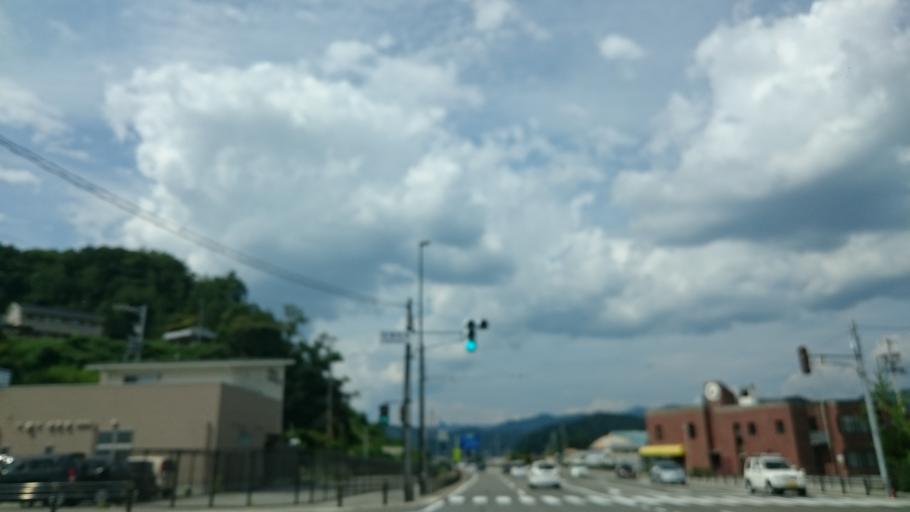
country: JP
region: Gifu
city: Takayama
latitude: 36.1580
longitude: 137.2437
